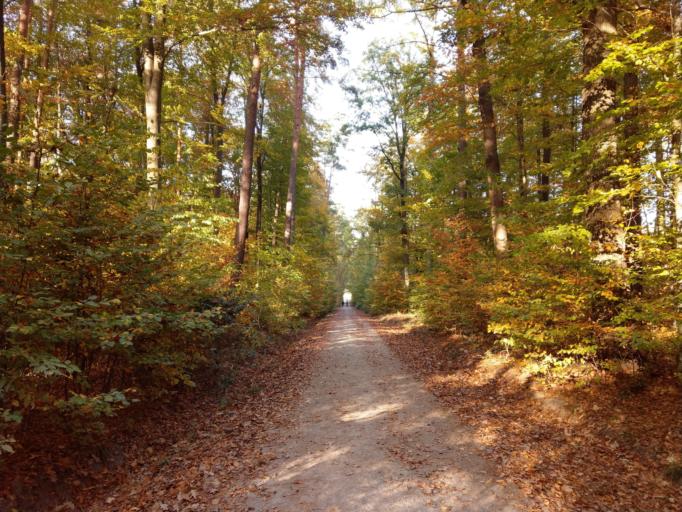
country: DE
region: Baden-Wuerttemberg
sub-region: Regierungsbezirk Stuttgart
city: Filderstadt
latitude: 48.6420
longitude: 9.1972
